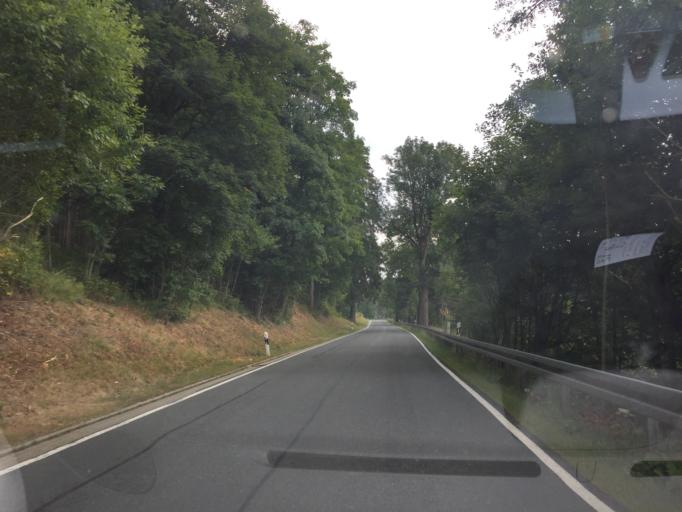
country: DE
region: Saxony-Anhalt
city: Benneckenstein
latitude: 51.7140
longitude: 10.7501
